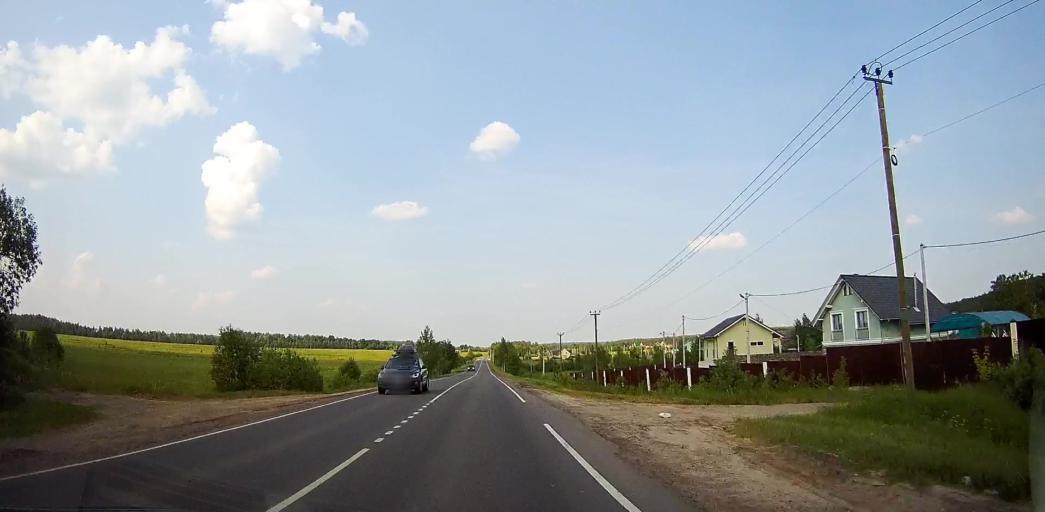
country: RU
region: Moskovskaya
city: Mikhnevo
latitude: 55.1718
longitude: 37.9637
